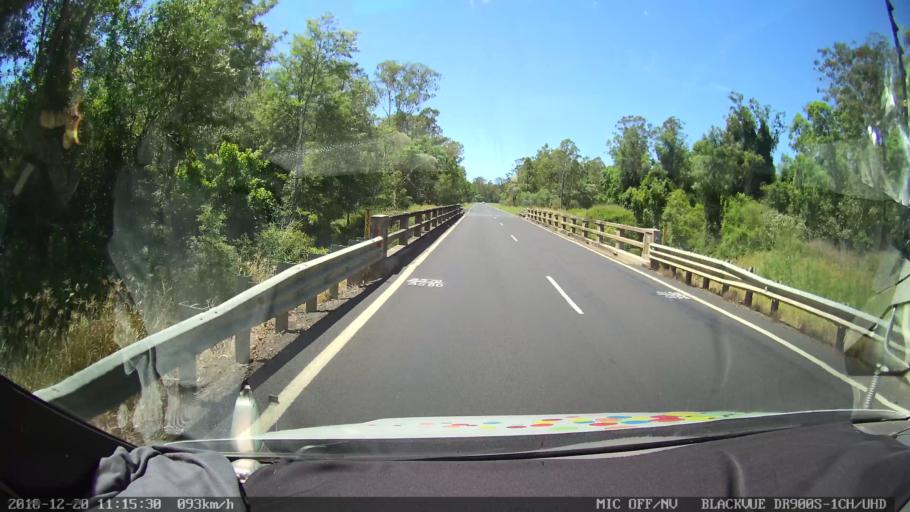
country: AU
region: New South Wales
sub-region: Richmond Valley
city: Casino
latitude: -29.0141
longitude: 153.0091
